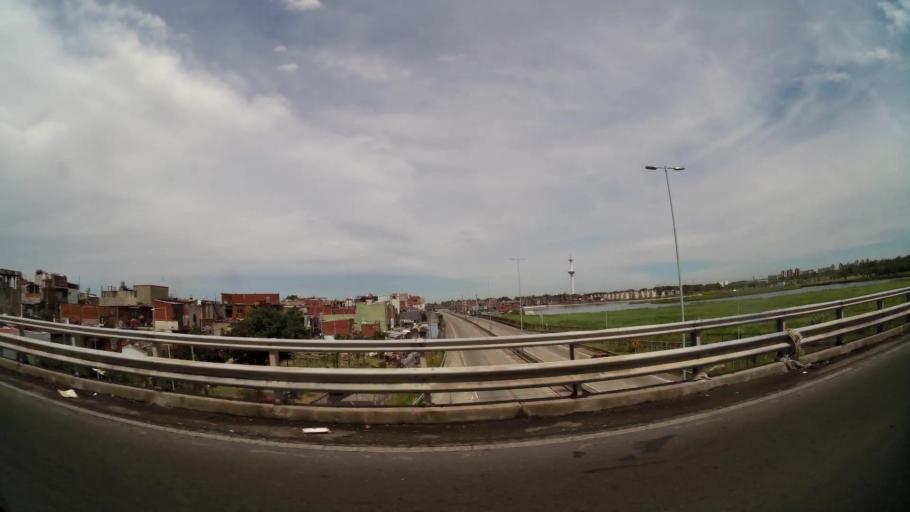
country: AR
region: Buenos Aires F.D.
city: Villa Lugano
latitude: -34.6567
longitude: -58.4600
